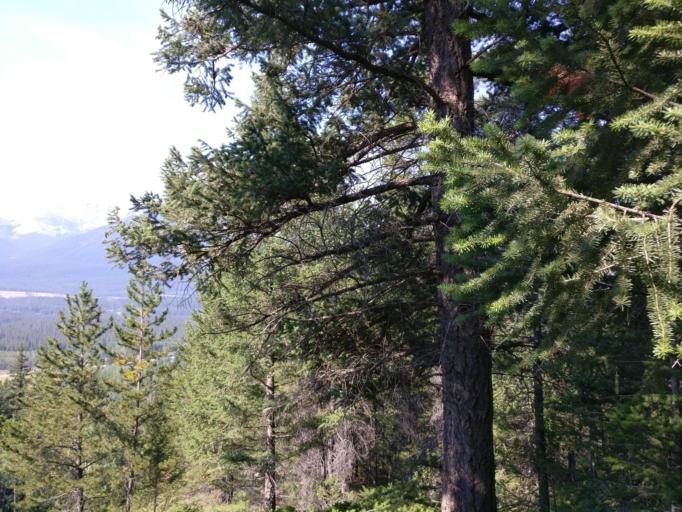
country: CA
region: Alberta
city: Canmore
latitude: 51.0802
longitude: -115.3115
